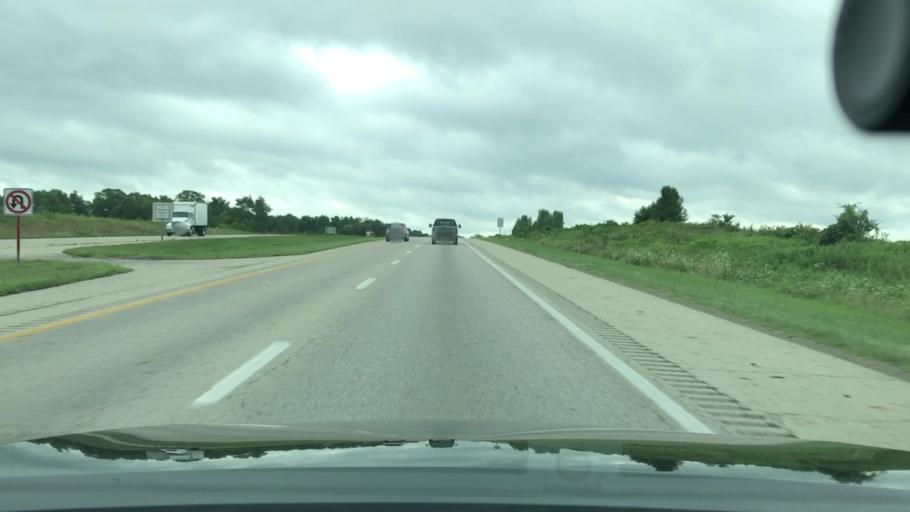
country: US
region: Ohio
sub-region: Ross County
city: Chillicothe
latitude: 39.2948
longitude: -82.9035
